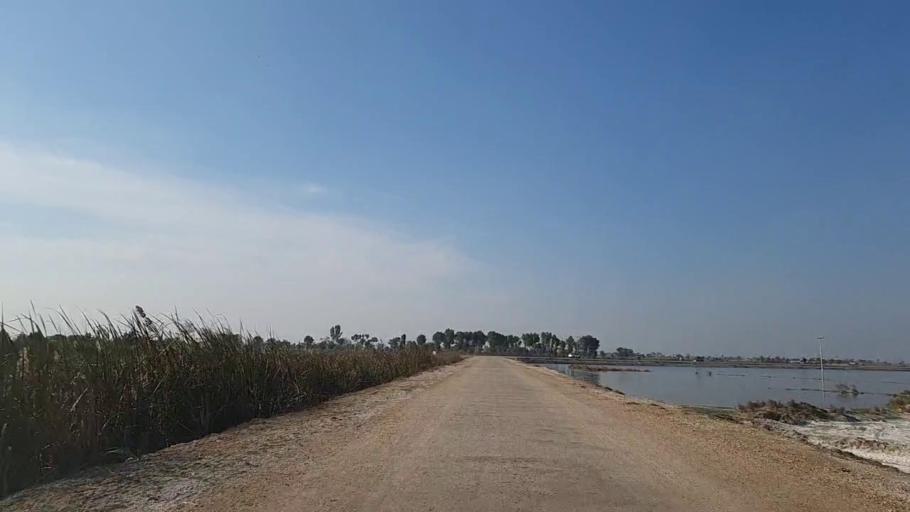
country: PK
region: Sindh
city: Bandhi
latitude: 26.6104
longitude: 68.3101
